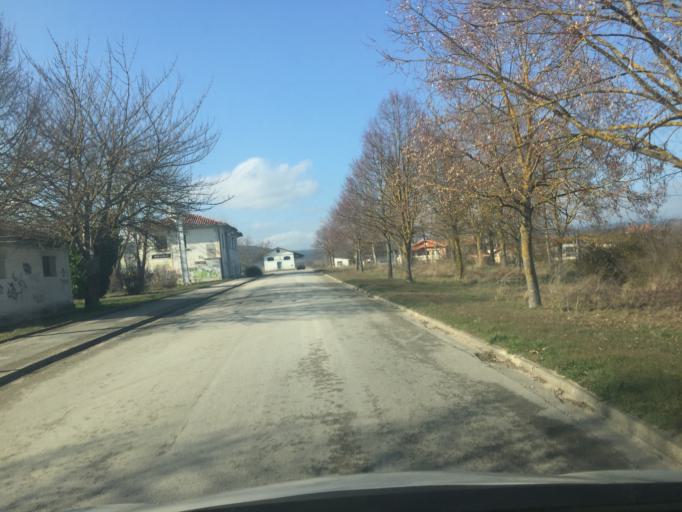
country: ES
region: Castille and Leon
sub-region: Provincia de Burgos
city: Medina de Pomar
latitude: 42.9279
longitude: -3.5788
